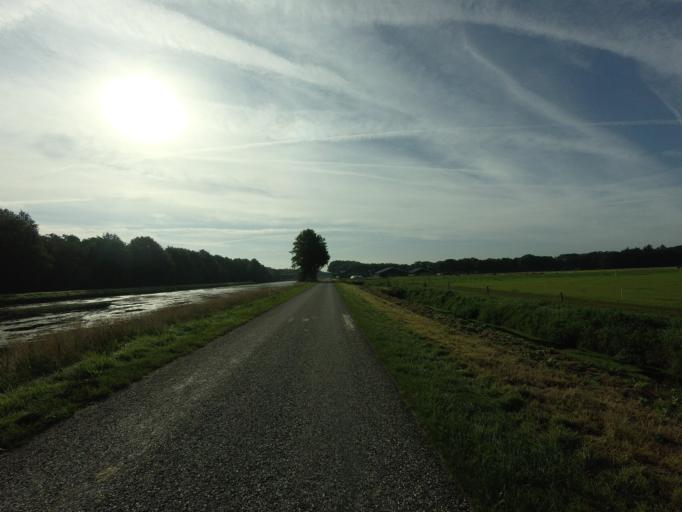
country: NL
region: Drenthe
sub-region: Gemeente Tynaarlo
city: Tynaarlo
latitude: 53.0644
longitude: 6.5990
